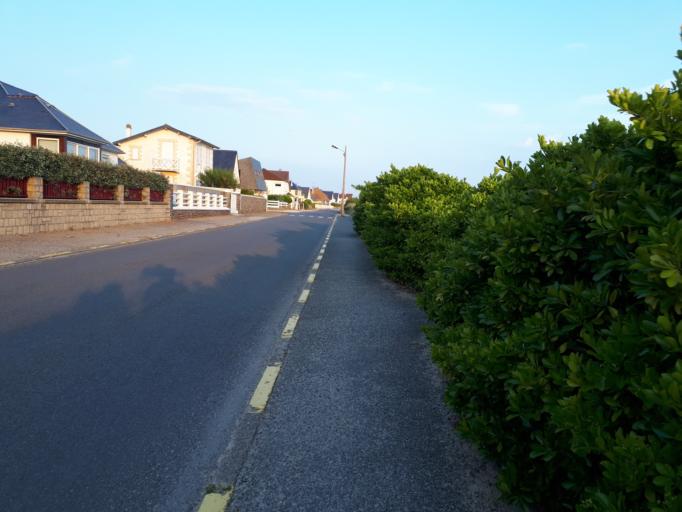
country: FR
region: Lower Normandy
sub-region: Departement de la Manche
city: Barneville-Plage
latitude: 49.3646
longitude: -1.7664
